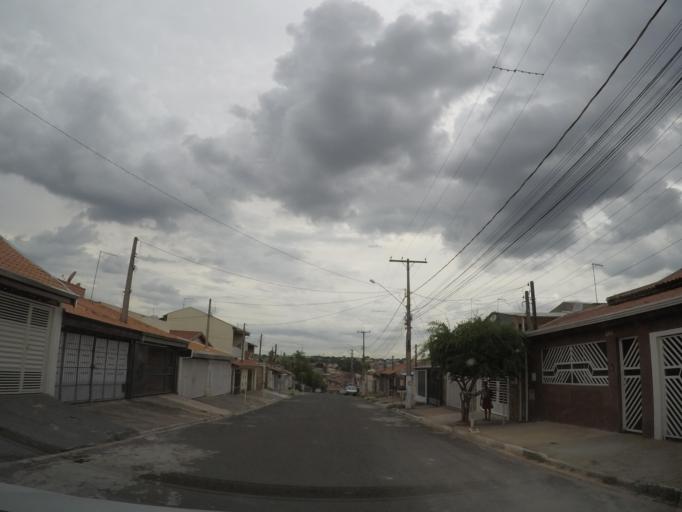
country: BR
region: Sao Paulo
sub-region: Sumare
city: Sumare
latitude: -22.8120
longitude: -47.2393
